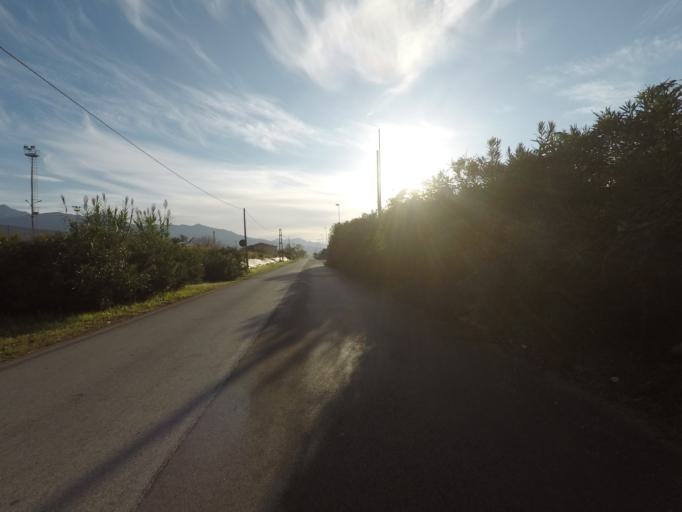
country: IT
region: Tuscany
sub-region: Provincia di Massa-Carrara
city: Massa
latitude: 44.0321
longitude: 10.1039
